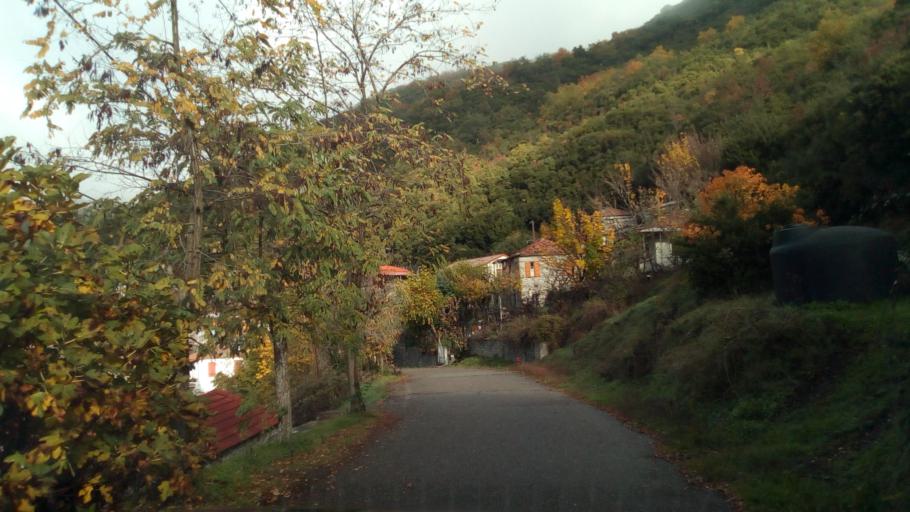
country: GR
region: West Greece
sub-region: Nomos Aitolias kai Akarnanias
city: Nafpaktos
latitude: 38.5142
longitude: 21.9575
